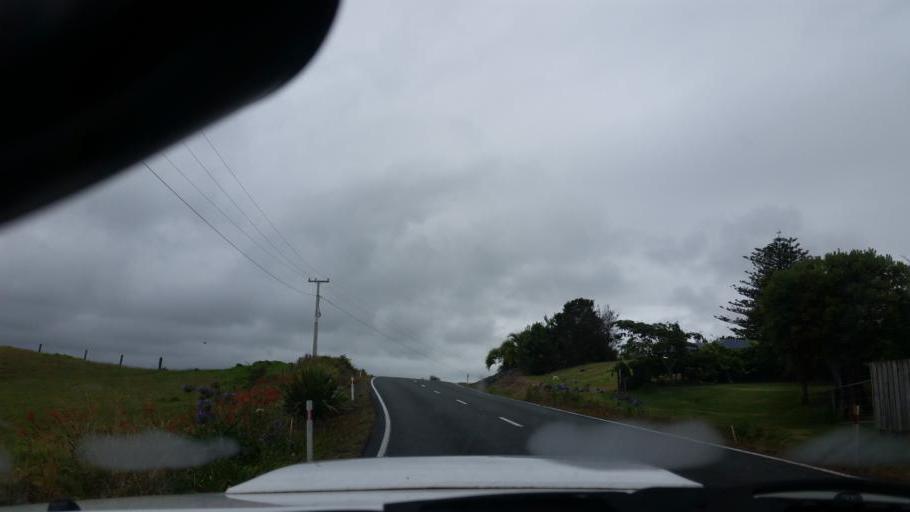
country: NZ
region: Auckland
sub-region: Auckland
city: Wellsford
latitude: -36.1595
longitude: 174.4538
